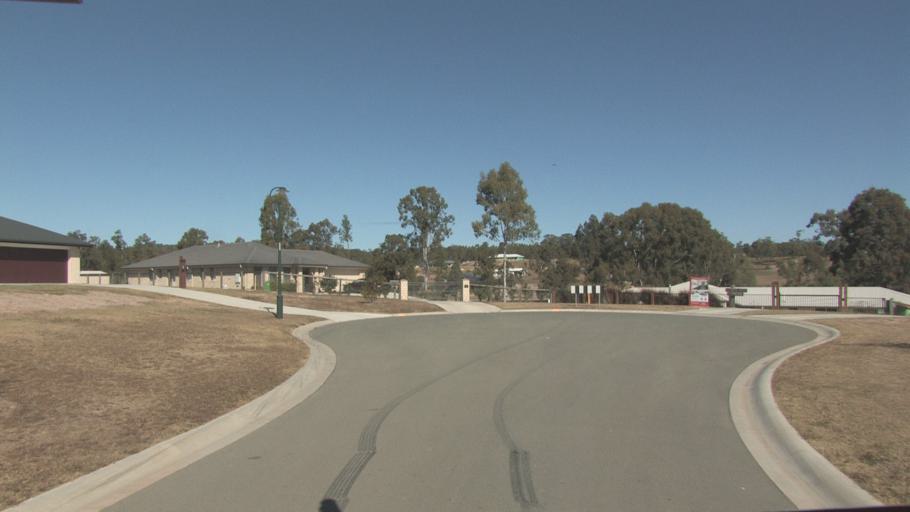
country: AU
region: Queensland
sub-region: Logan
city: Cedar Vale
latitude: -27.8700
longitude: 153.0438
